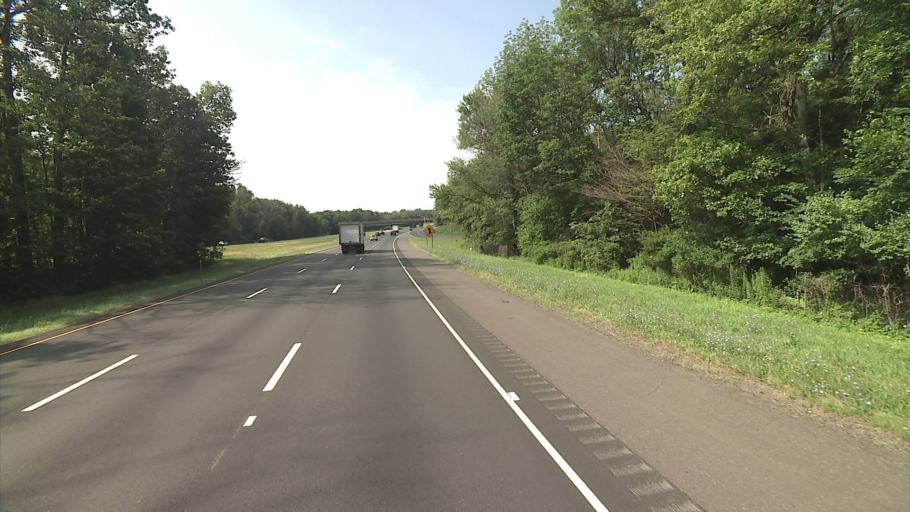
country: US
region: Connecticut
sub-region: New Haven County
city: Wallingford Center
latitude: 41.4584
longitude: -72.7788
